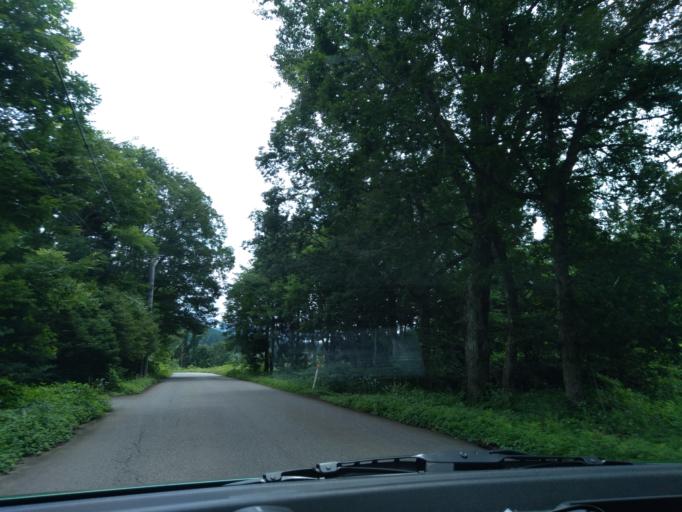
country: JP
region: Akita
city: Kakunodatemachi
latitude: 39.5737
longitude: 140.6309
